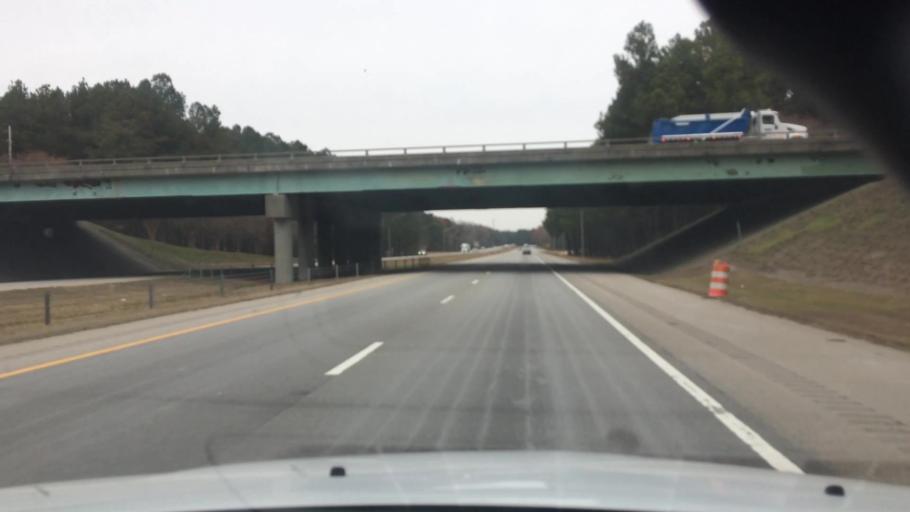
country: US
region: North Carolina
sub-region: Wilson County
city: Wilson
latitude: 35.7628
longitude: -78.0040
